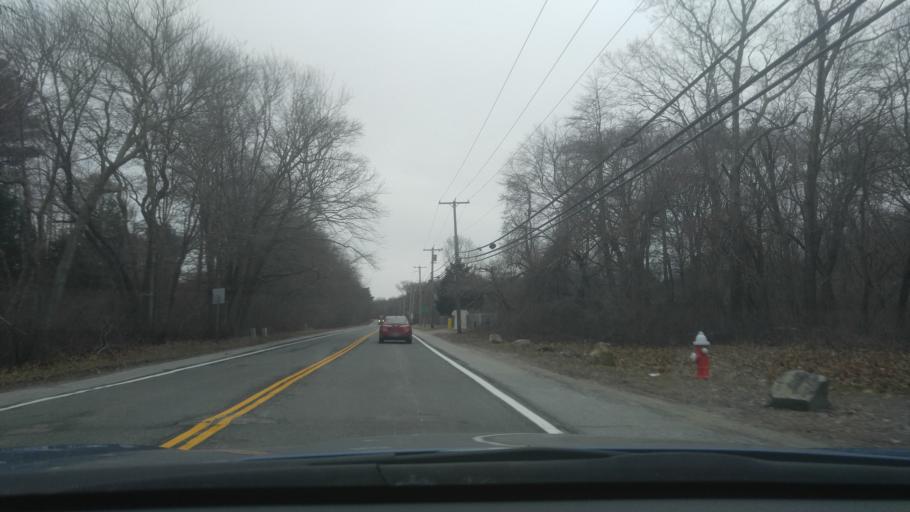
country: US
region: Rhode Island
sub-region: Washington County
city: North Kingstown
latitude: 41.5036
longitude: -71.4303
